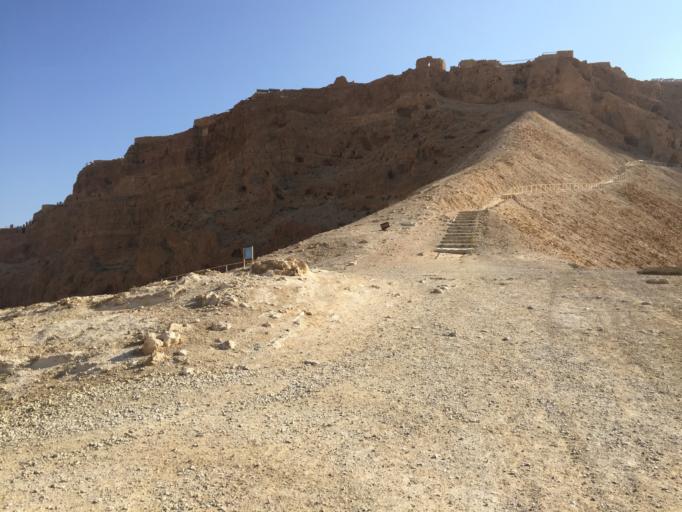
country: IL
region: Southern District
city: `En Boqeq
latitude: 31.3170
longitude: 35.3509
